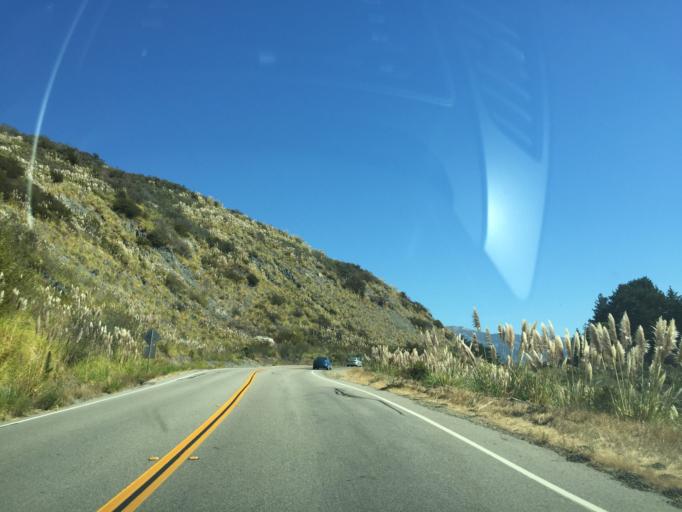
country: US
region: California
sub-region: Monterey County
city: Greenfield
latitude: 36.0219
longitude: -121.5538
